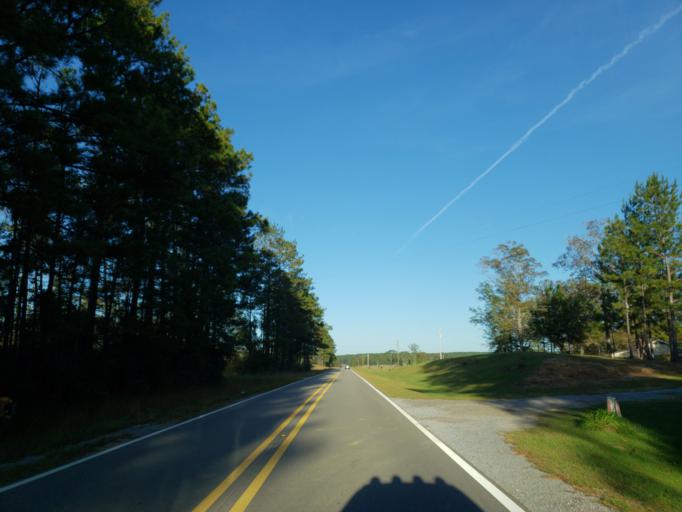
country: US
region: Mississippi
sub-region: Perry County
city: Richton
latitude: 31.3610
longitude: -88.7304
